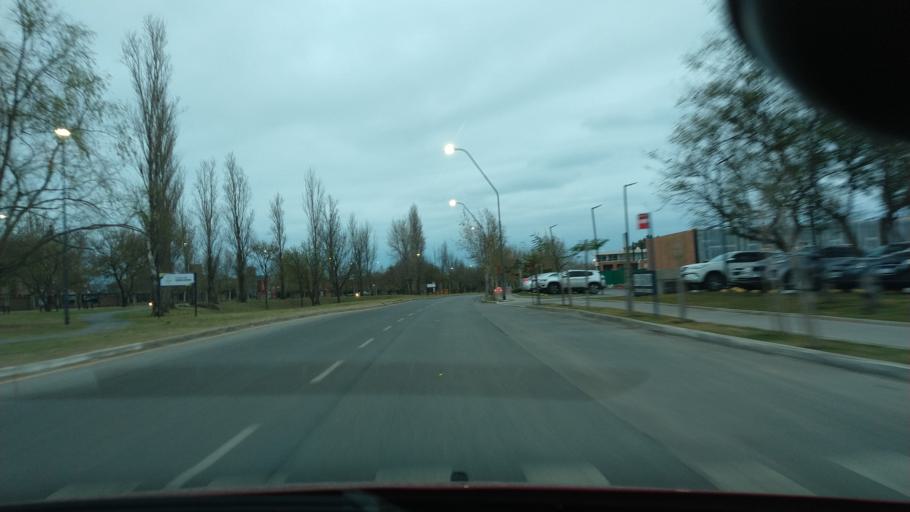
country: AR
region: Cordoba
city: La Calera
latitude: -31.3731
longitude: -64.2774
